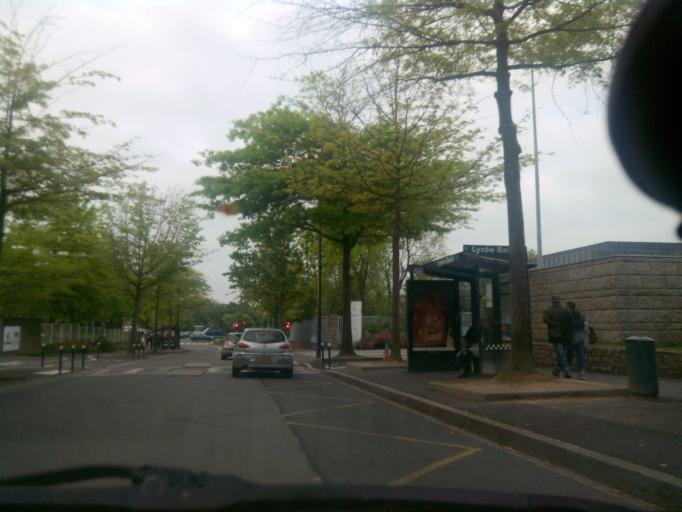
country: FR
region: Brittany
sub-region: Departement d'Ille-et-Vilaine
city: Saint-Gregoire
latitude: 48.1274
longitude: -1.6934
